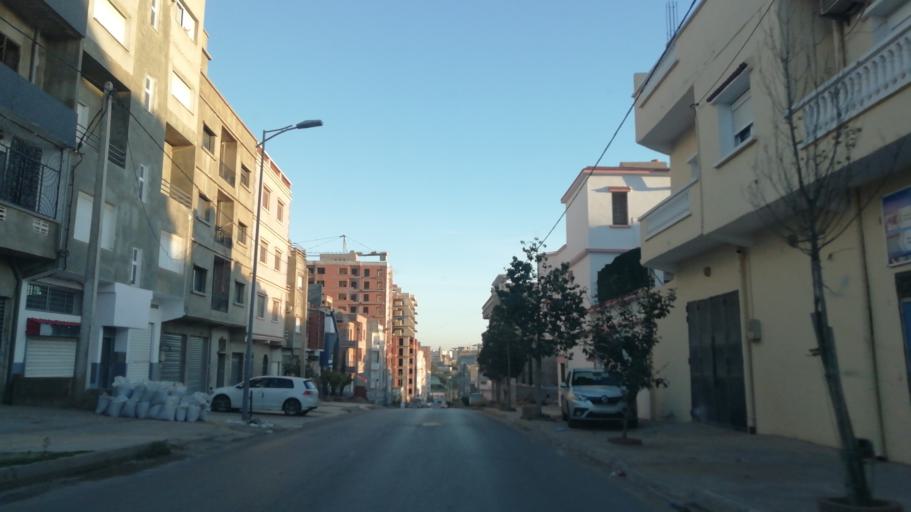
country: DZ
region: Oran
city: Bir el Djir
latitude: 35.7200
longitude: -0.5774
